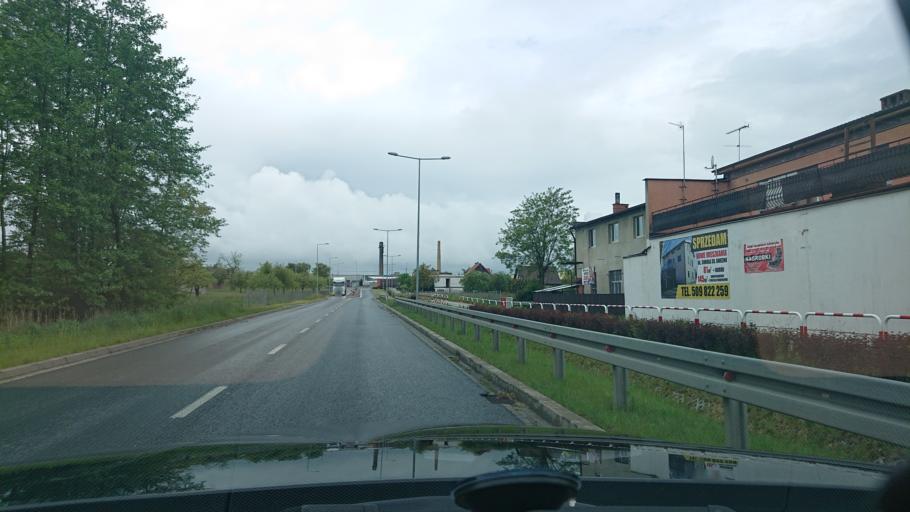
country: PL
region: Greater Poland Voivodeship
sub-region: Powiat gnieznienski
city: Gniezno
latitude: 52.5184
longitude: 17.6129
